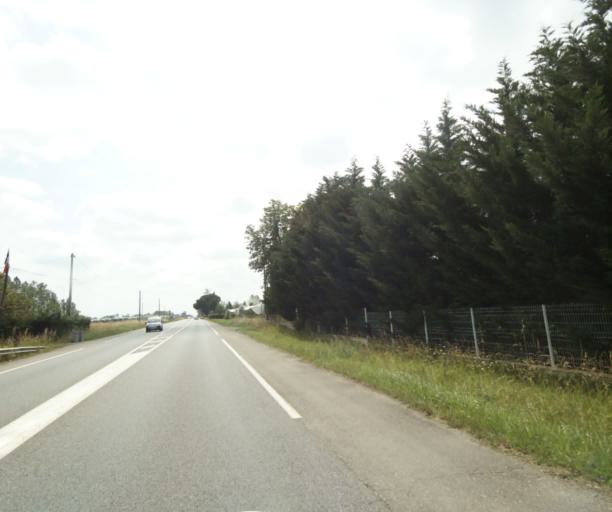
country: FR
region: Midi-Pyrenees
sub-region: Departement du Tarn-et-Garonne
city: Albias
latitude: 44.0683
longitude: 1.4193
